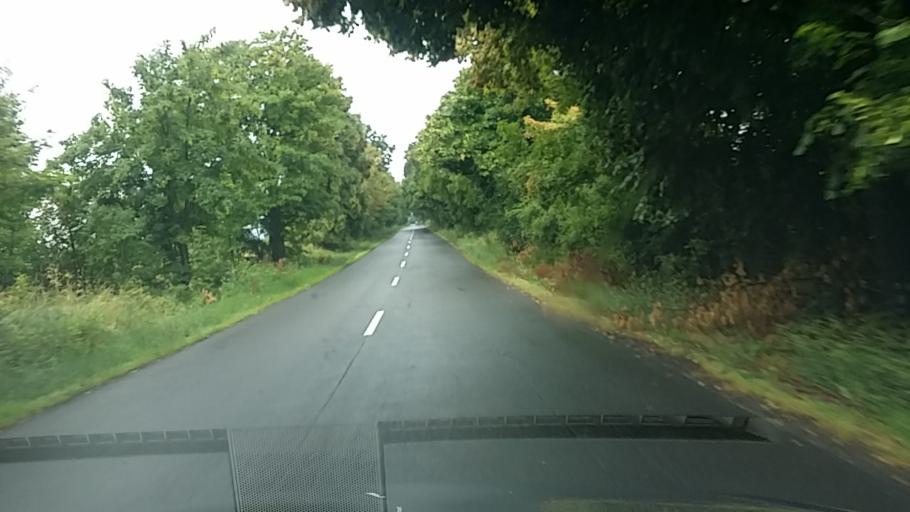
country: SK
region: Nitriansky
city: Sahy
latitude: 47.9949
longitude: 18.8349
